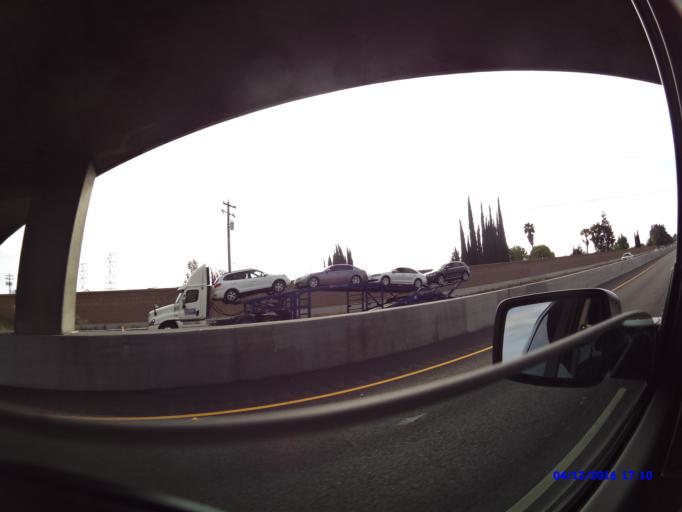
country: US
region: California
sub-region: San Joaquin County
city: Manteca
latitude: 37.8071
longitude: -121.1985
